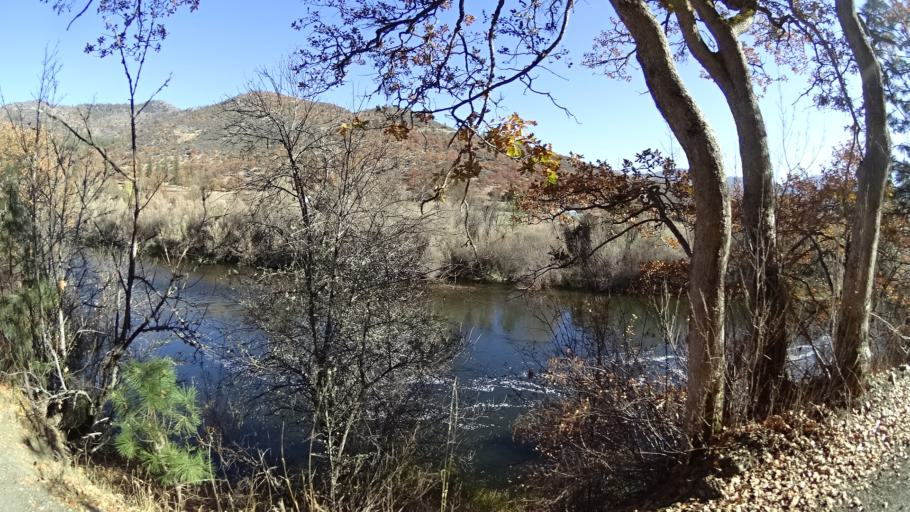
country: US
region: California
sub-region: Siskiyou County
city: Yreka
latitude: 41.8375
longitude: -122.8716
